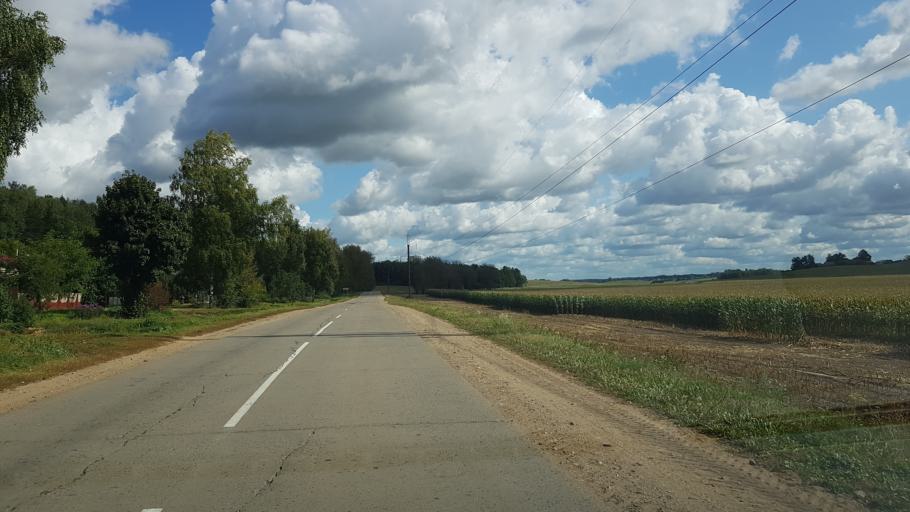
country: BY
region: Minsk
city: Dzyarzhynsk
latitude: 53.7357
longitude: 27.2281
